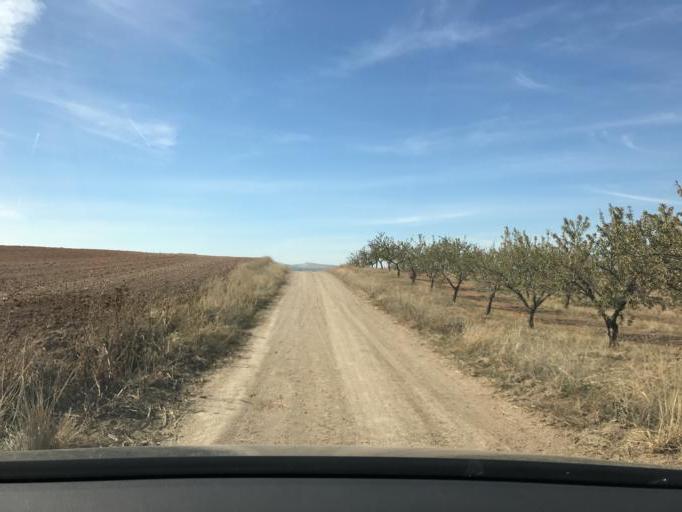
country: ES
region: Andalusia
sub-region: Provincia de Granada
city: Ventas de Huelma
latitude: 37.0887
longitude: -3.7890
